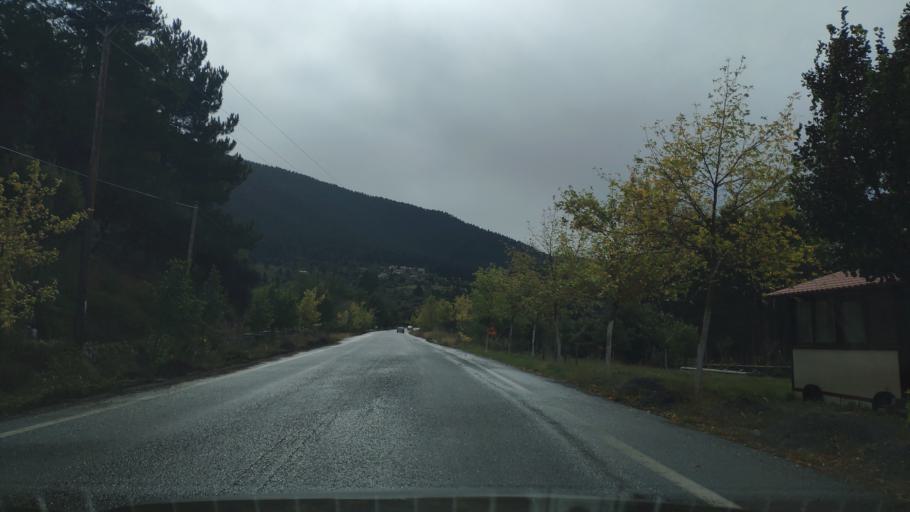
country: GR
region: Peloponnese
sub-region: Nomos Arkadias
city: Langadhia
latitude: 37.6721
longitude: 22.1932
